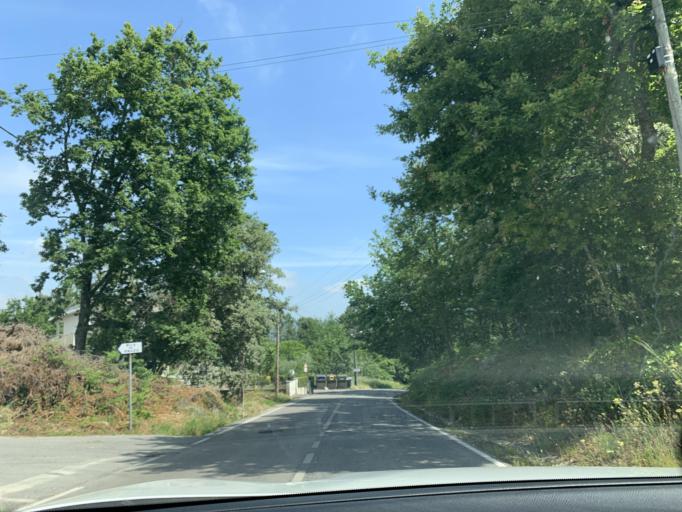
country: PT
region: Viseu
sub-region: Viseu
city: Viseu
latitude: 40.6465
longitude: -7.9410
